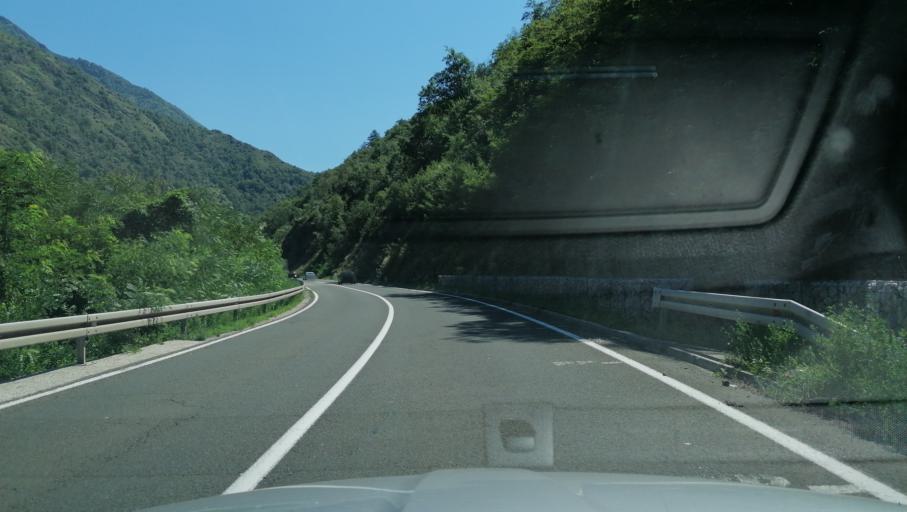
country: RS
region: Central Serbia
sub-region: Raski Okrug
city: Kraljevo
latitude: 43.5894
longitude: 20.5735
